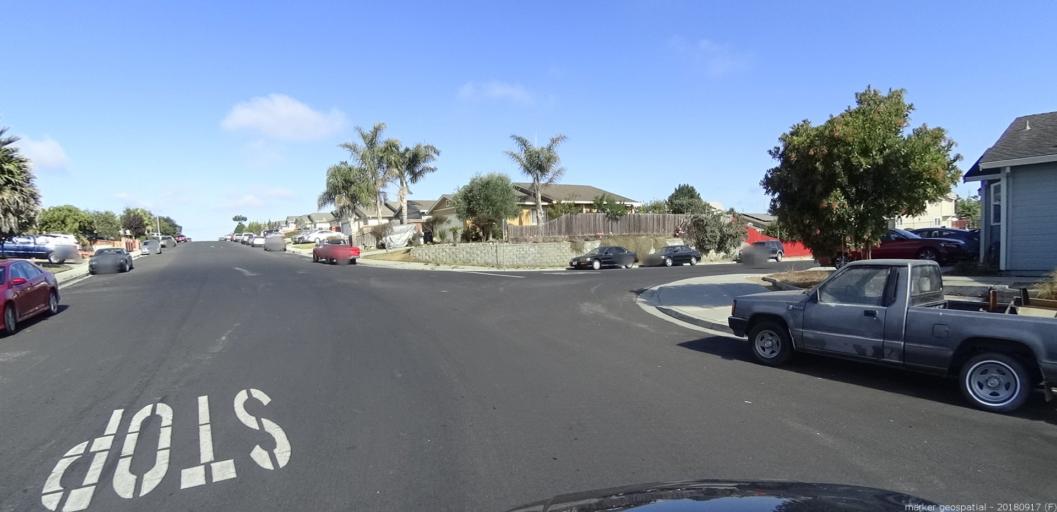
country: US
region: California
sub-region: Monterey County
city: Castroville
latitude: 36.7869
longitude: -121.7264
